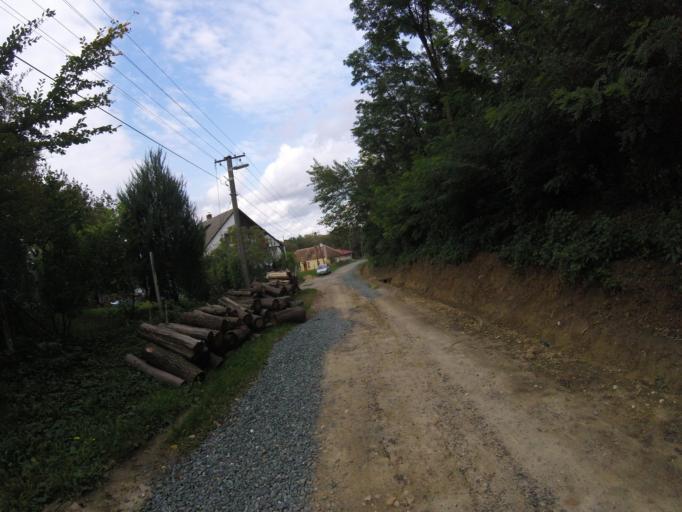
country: HU
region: Vas
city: Csepreg
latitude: 47.3591
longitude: 16.6742
